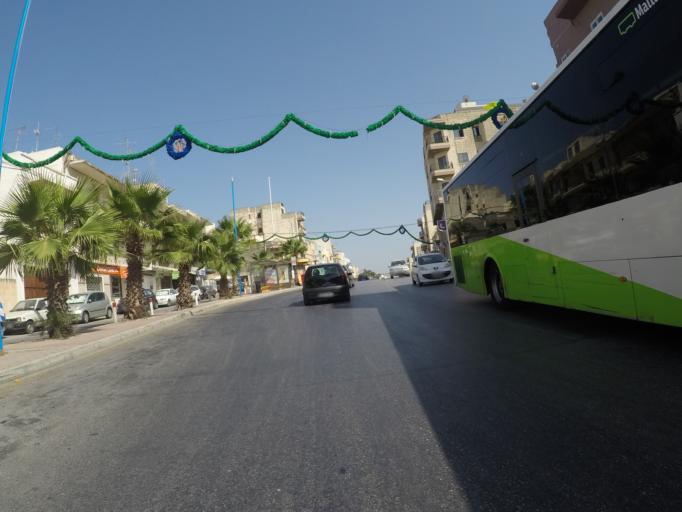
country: MT
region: Saint Paul's Bay
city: San Pawl il-Bahar
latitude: 35.9468
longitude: 14.4082
